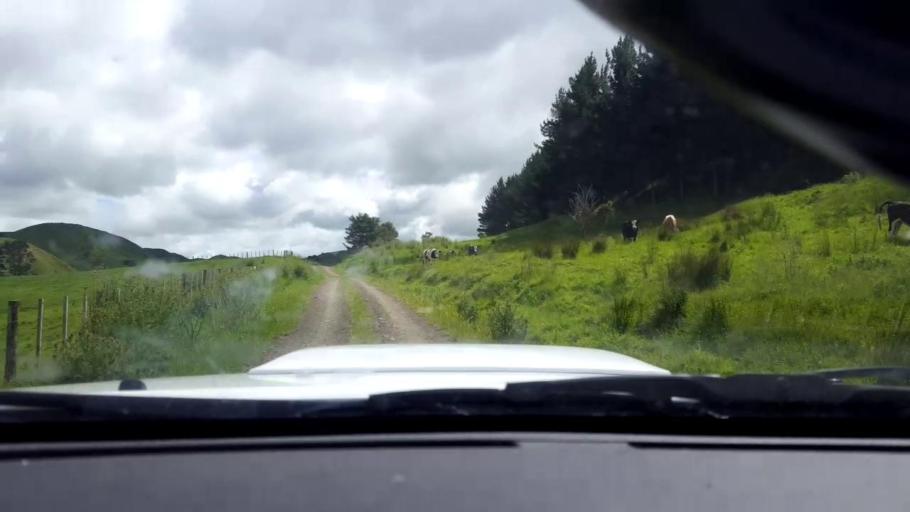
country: NZ
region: Gisborne
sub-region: Gisborne District
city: Gisborne
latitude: -38.4910
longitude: 177.6760
